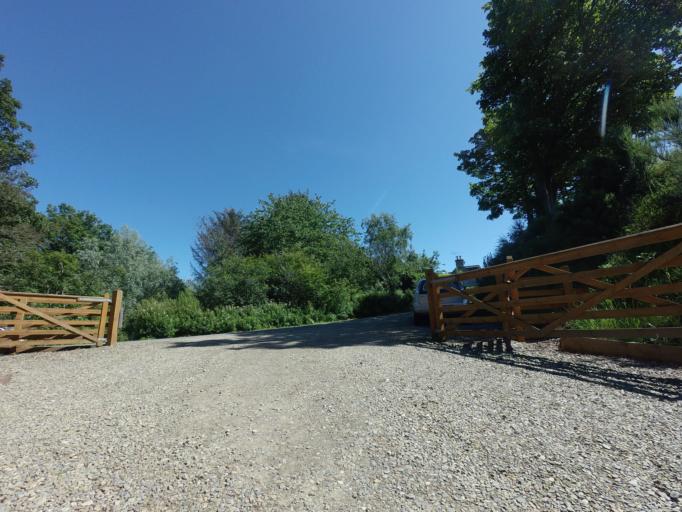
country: GB
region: Scotland
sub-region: Aberdeenshire
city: Macduff
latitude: 57.6324
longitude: -2.4876
